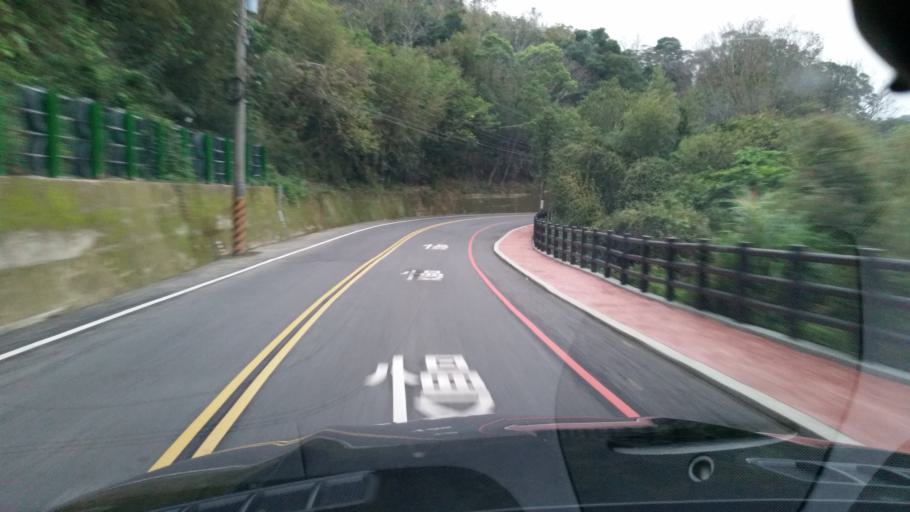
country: TW
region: Taiwan
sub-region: Miaoli
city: Miaoli
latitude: 24.5796
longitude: 120.8846
